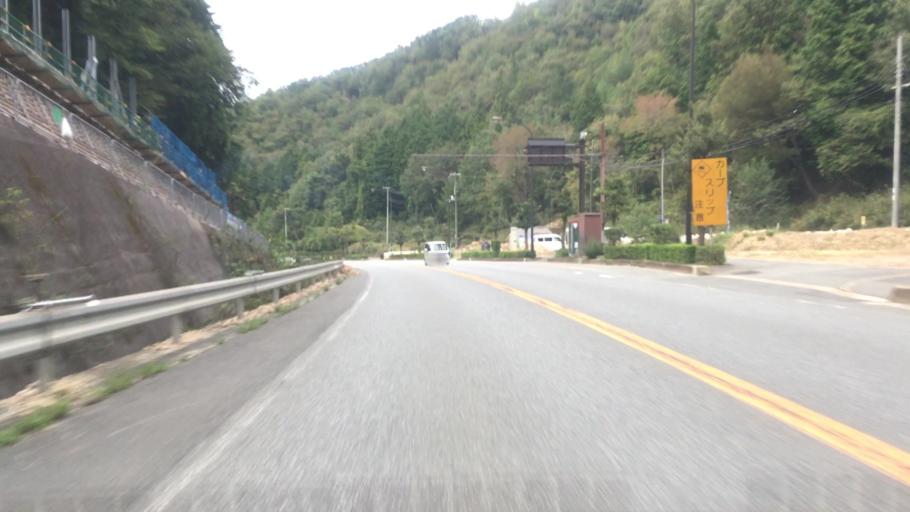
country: JP
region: Hyogo
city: Toyooka
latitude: 35.3958
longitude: 134.7726
